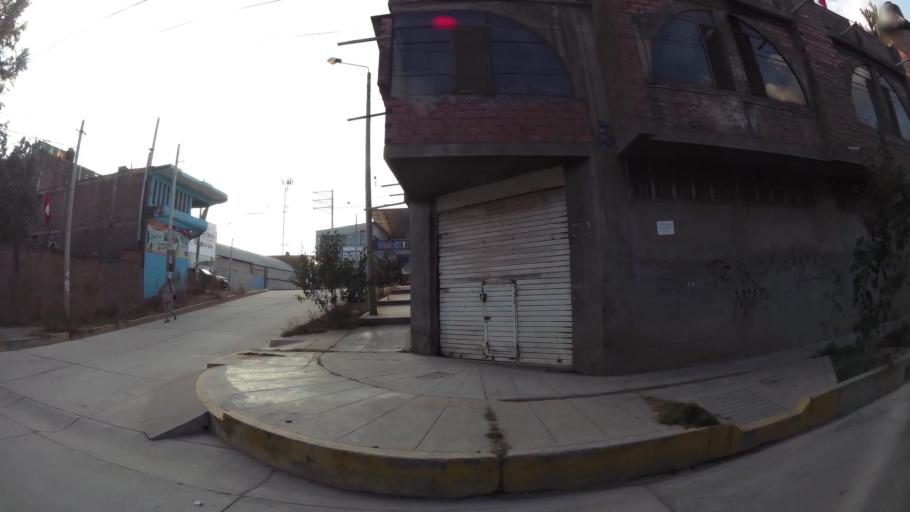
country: PE
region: Junin
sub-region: Provincia de Huancayo
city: Pilcomay
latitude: -12.0447
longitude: -75.2274
